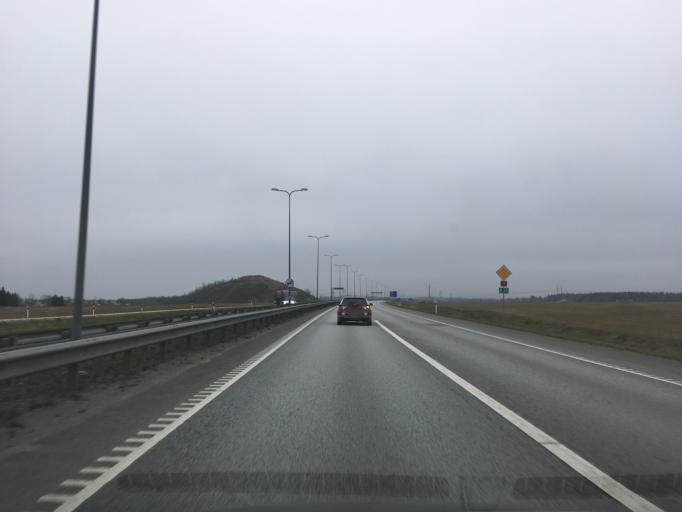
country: EE
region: Ida-Virumaa
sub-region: Kohtla-Jaerve linn
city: Kohtla-Jarve
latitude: 59.4002
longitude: 27.3311
